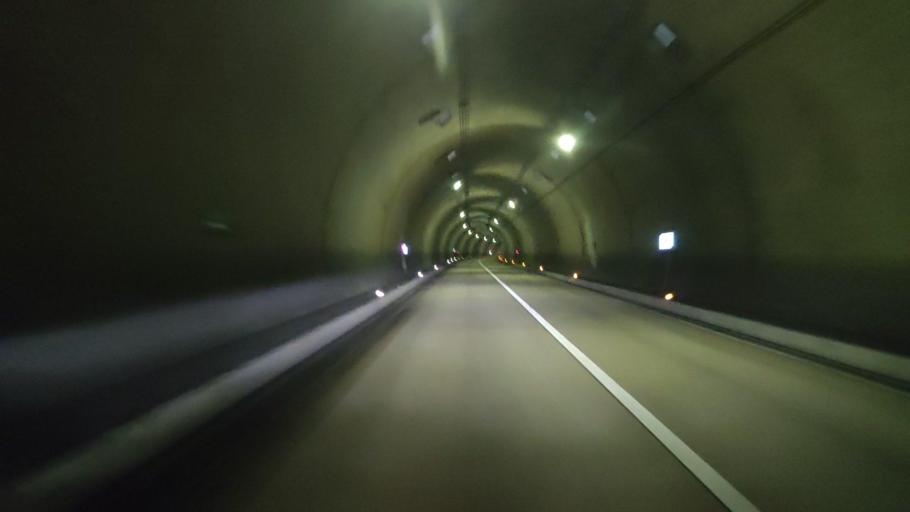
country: JP
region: Wakayama
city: Shingu
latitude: 33.8514
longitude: 135.8565
